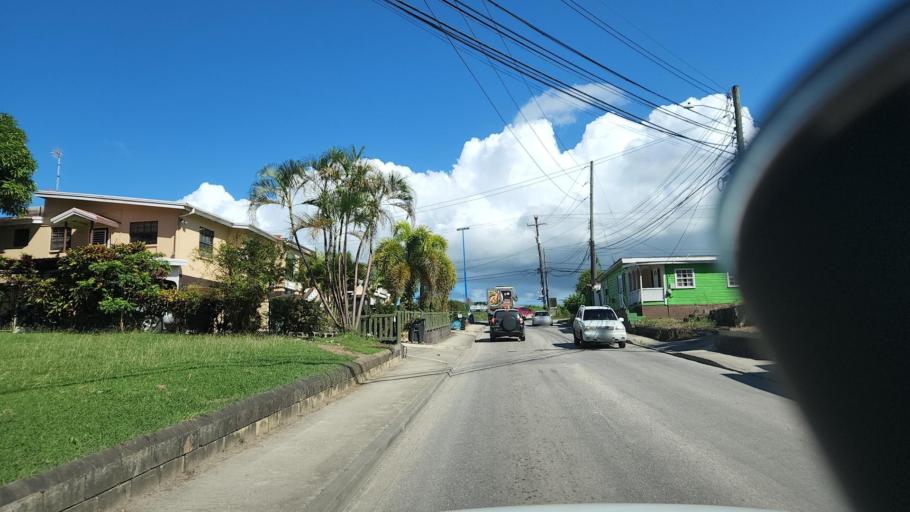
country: BB
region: Saint Thomas
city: Welchman Hall
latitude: 13.1473
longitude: -59.5918
